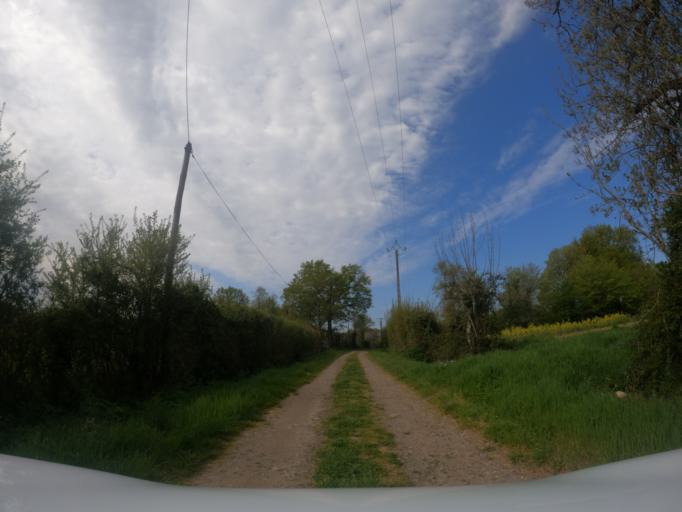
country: FR
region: Pays de la Loire
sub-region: Departement de la Vendee
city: Le Champ-Saint-Pere
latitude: 46.5188
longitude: -1.3372
